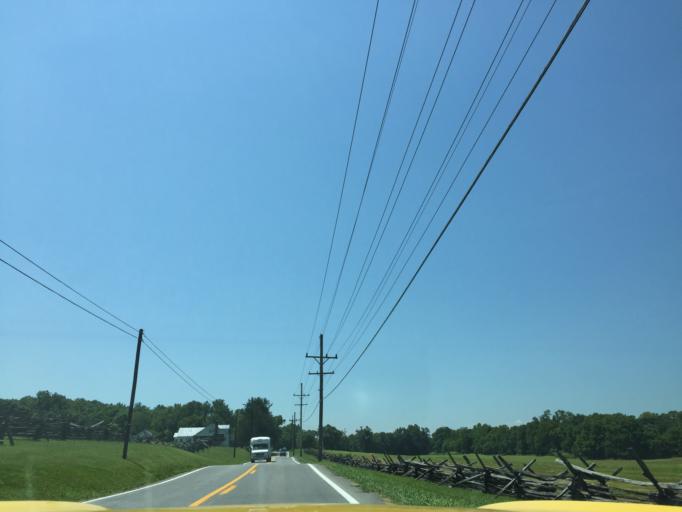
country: US
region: West Virginia
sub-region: Jefferson County
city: Bolivar
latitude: 39.3233
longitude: -77.7679
